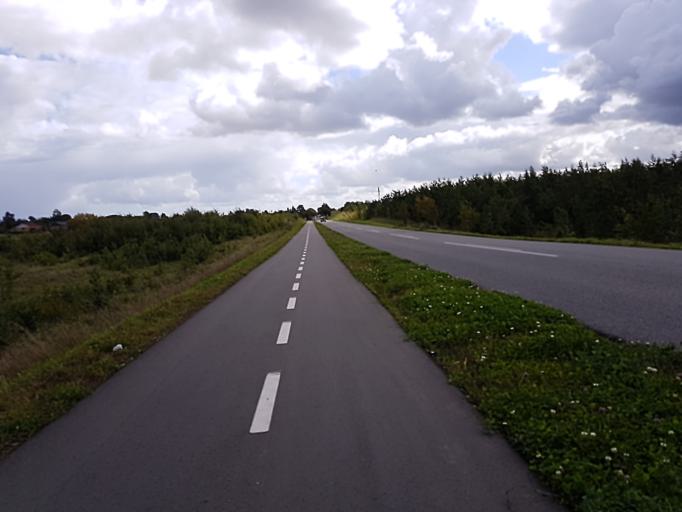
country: DK
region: Zealand
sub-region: Roskilde Kommune
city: Gundsomagle
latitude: 55.7438
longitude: 12.1454
